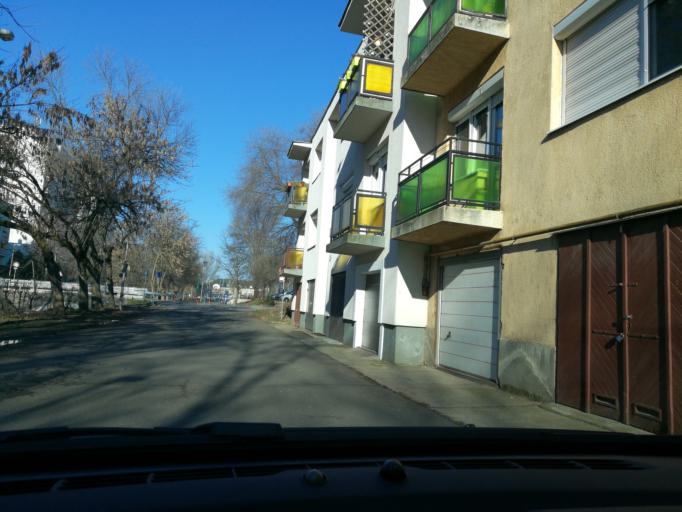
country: HU
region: Szabolcs-Szatmar-Bereg
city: Nyiregyhaza
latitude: 47.9425
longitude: 21.7129
